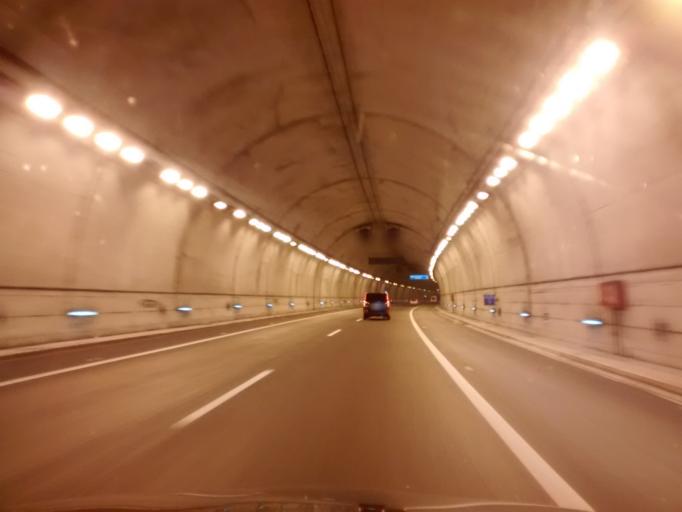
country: ES
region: Cantabria
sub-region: Provincia de Cantabria
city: Camargo
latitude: 43.3972
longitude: -3.8677
